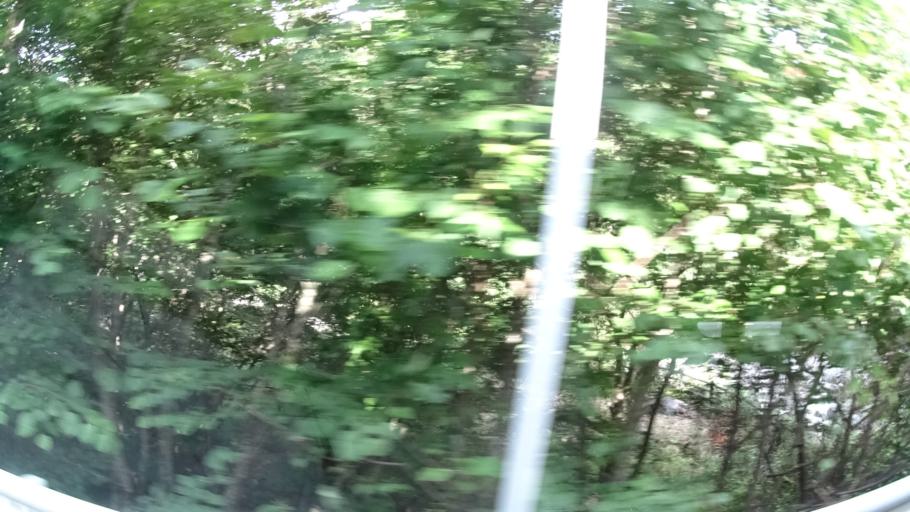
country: JP
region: Tochigi
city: Nikko
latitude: 36.6878
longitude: 139.4979
